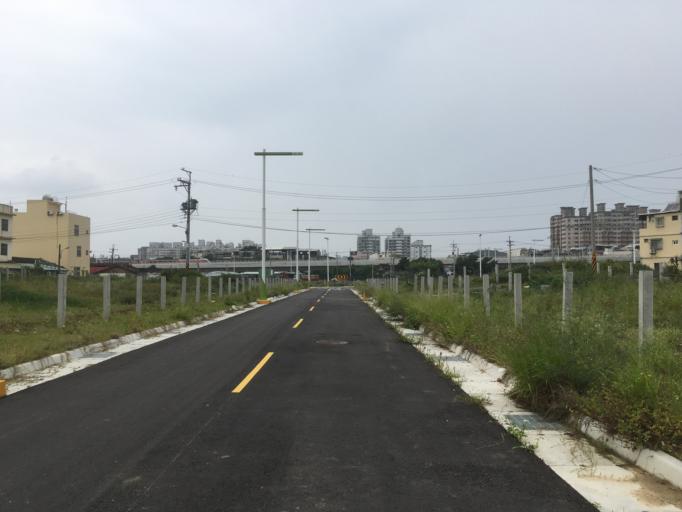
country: TW
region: Taiwan
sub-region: Taichung City
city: Taichung
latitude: 24.1859
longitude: 120.7055
